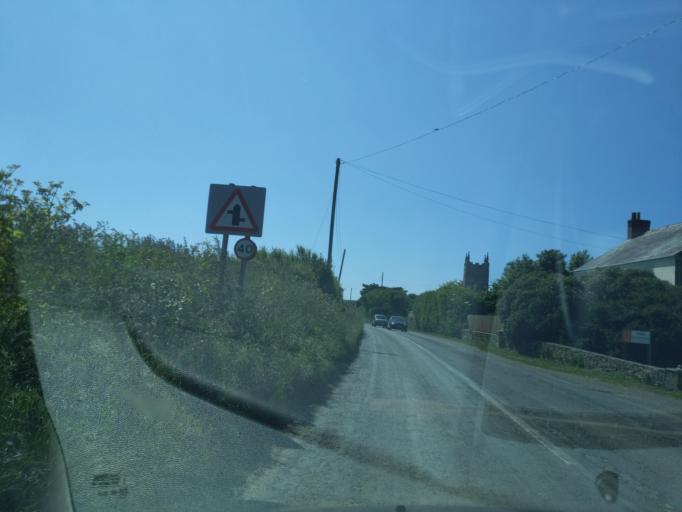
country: GB
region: England
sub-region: Cornwall
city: Wadebridge
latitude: 50.5733
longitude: -4.8282
